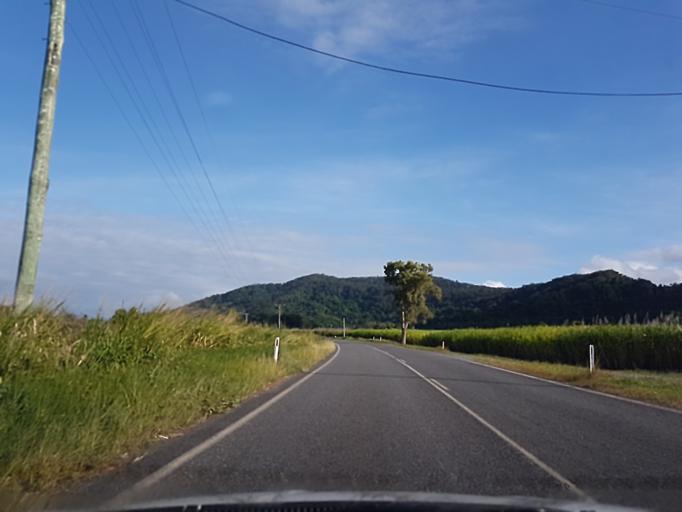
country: AU
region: Queensland
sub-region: Cairns
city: Port Douglas
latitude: -16.3412
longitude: 145.4093
